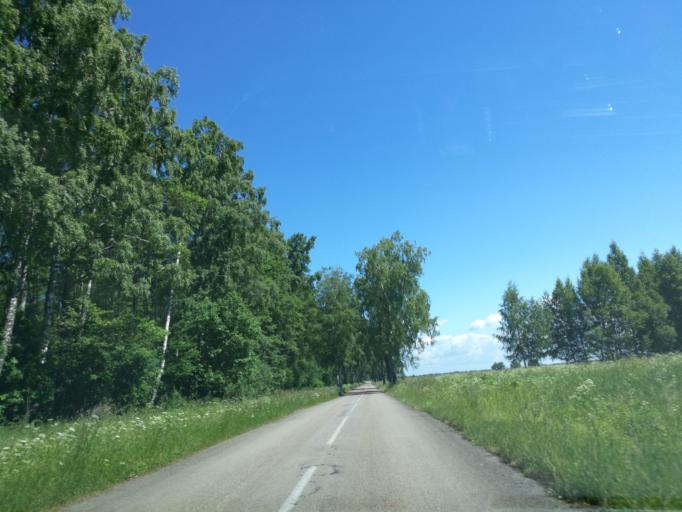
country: LT
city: Rusne
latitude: 55.3839
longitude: 21.2332
